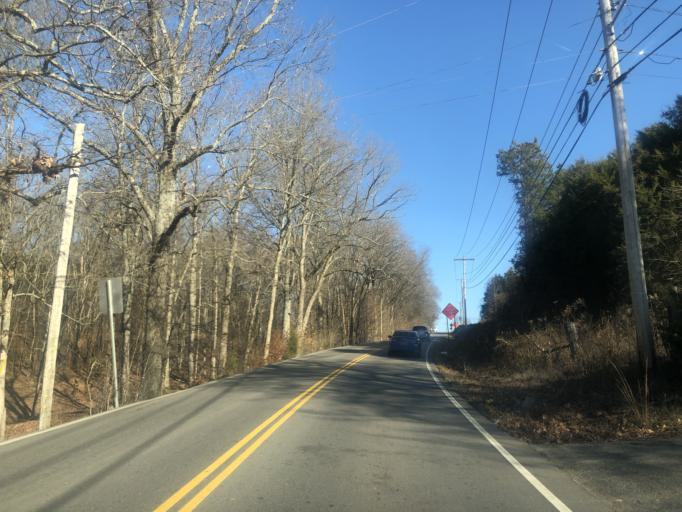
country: US
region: Tennessee
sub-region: Williamson County
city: Nolensville
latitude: 36.0297
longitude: -86.6624
